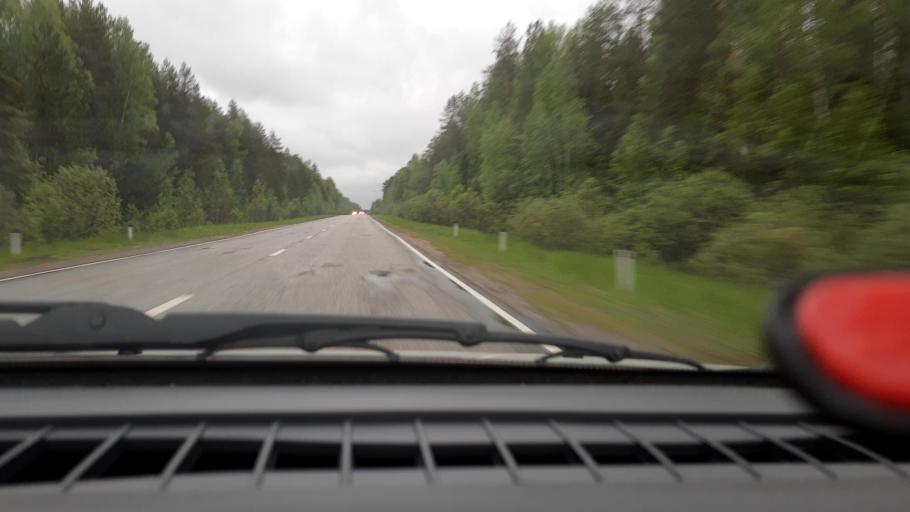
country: RU
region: Nizjnij Novgorod
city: Krasnyye Baki
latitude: 57.1842
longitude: 45.3908
